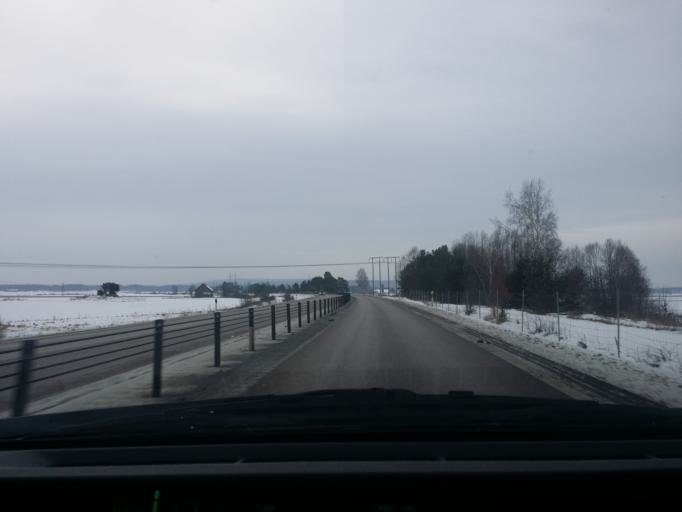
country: SE
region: Vaestra Goetaland
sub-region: Skovde Kommun
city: Stopen
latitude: 58.5714
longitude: 13.7990
